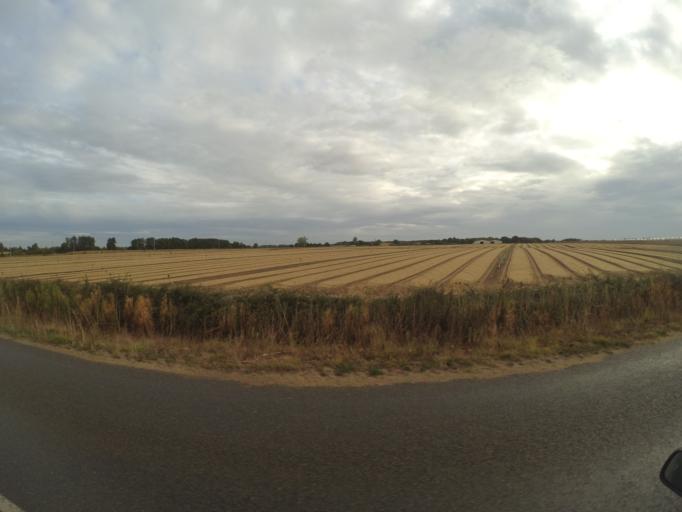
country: FR
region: Pays de la Loire
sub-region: Departement de la Loire-Atlantique
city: La Planche
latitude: 47.0266
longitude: -1.4585
